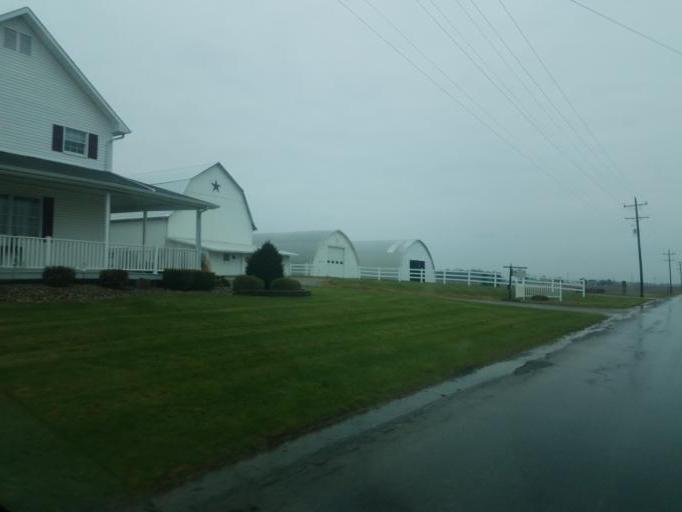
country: US
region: Ohio
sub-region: Knox County
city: Centerburg
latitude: 40.2450
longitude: -82.7221
